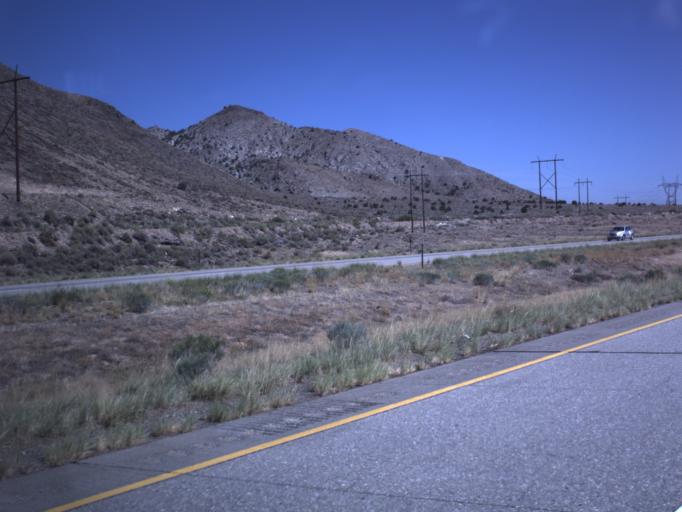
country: US
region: Utah
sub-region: Sevier County
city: Richfield
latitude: 38.7298
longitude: -112.1245
